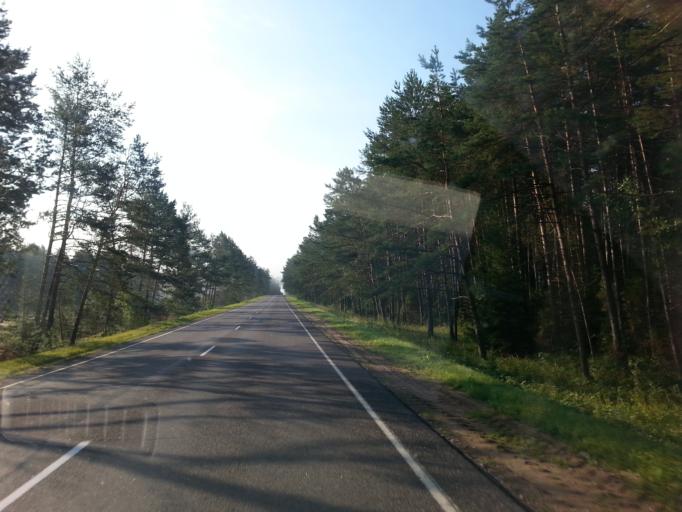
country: BY
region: Minsk
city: Kryvichy
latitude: 54.7458
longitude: 27.1212
